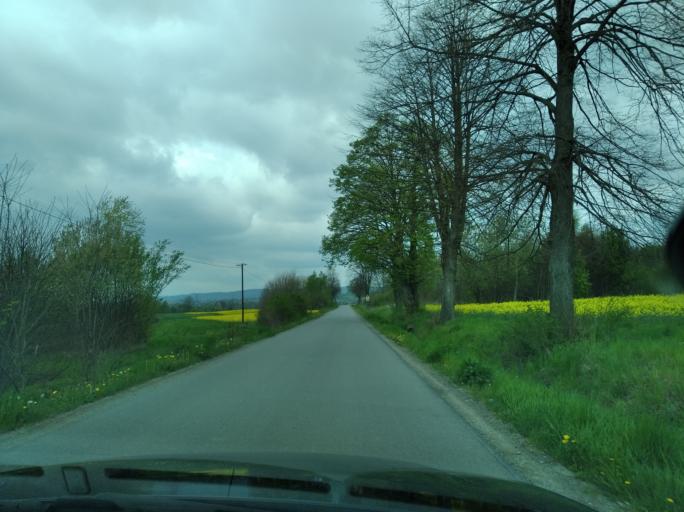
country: PL
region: Subcarpathian Voivodeship
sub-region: Powiat brzozowski
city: Jablonica Polska
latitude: 49.6873
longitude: 21.8935
